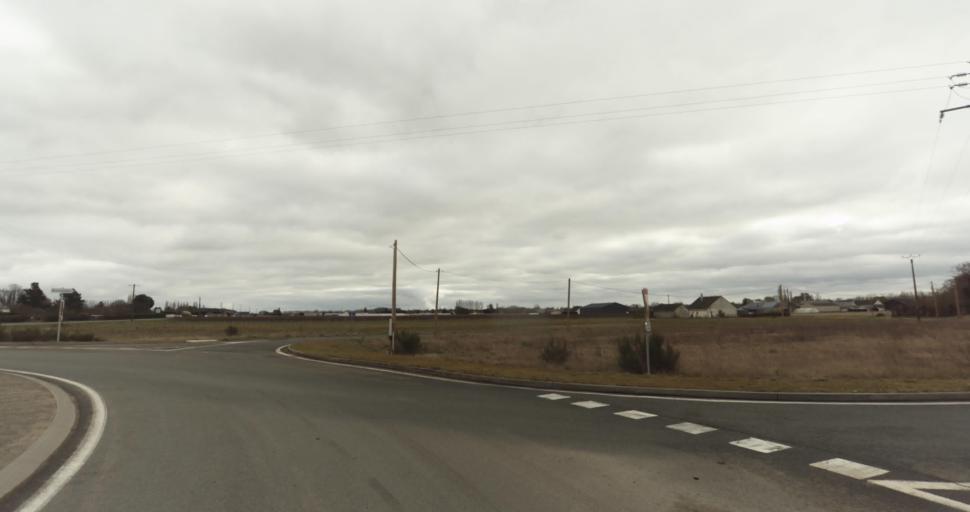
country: FR
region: Pays de la Loire
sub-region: Departement de Maine-et-Loire
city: Allonnes
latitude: 47.2905
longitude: 0.0352
